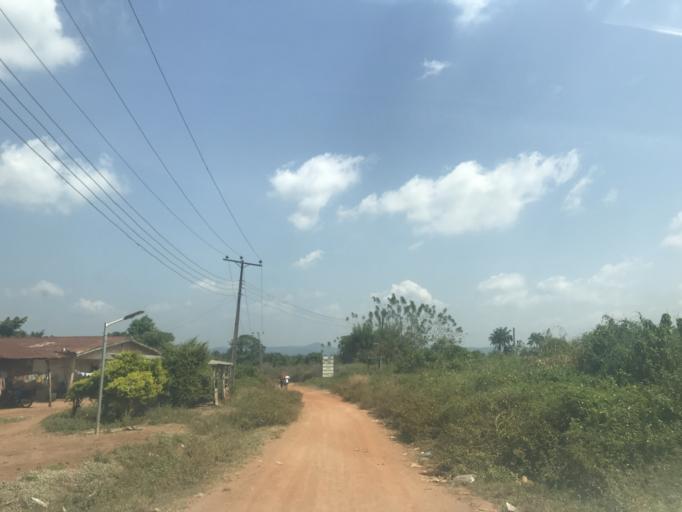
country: NG
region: Osun
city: Oke Mesi
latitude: 7.8866
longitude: 4.8883
